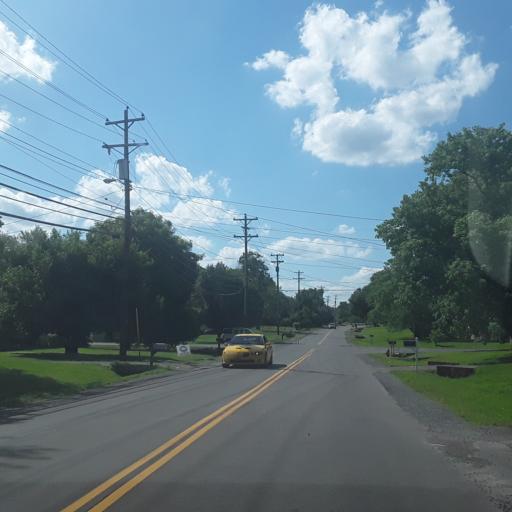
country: US
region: Tennessee
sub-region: Davidson County
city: Lakewood
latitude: 36.1952
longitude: -86.6275
